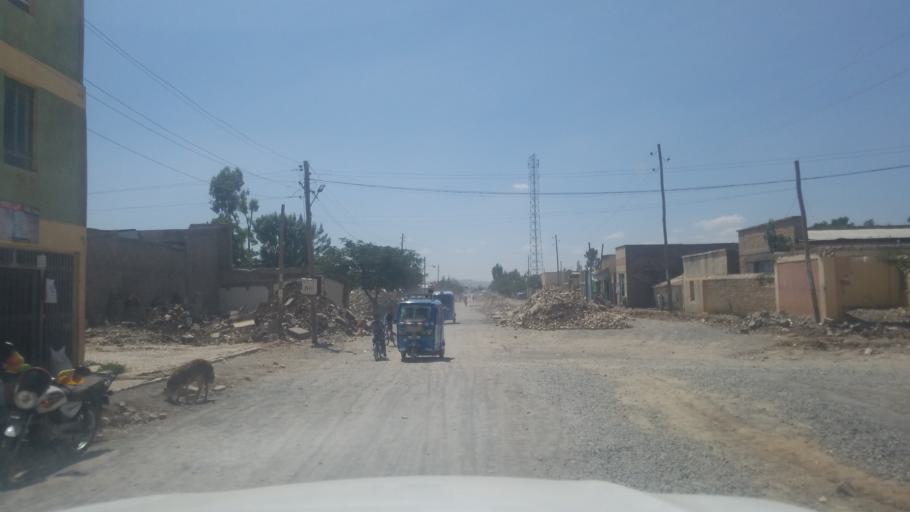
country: ET
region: Tigray
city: Mekele
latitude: 13.7905
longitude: 39.5985
